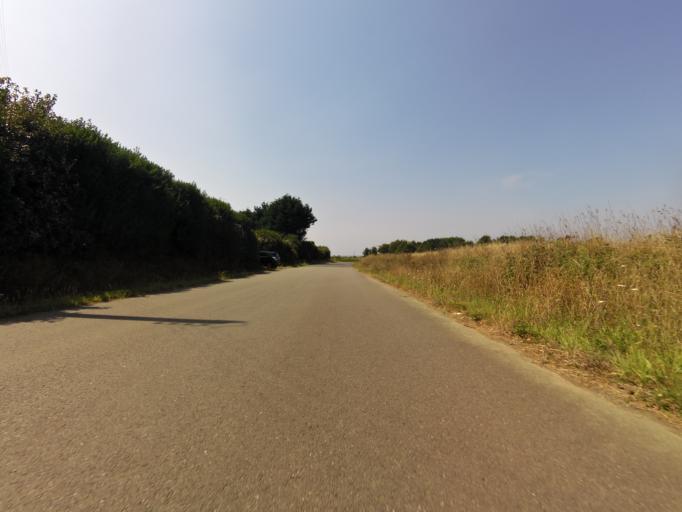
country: FR
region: Brittany
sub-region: Departement du Finistere
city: Pouldreuzic
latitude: 47.9072
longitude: -4.3483
